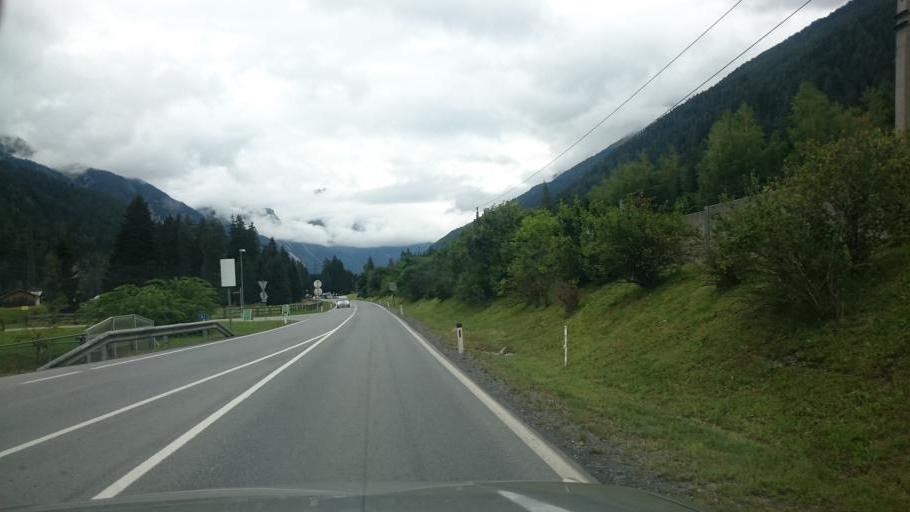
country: AT
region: Tyrol
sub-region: Politischer Bezirk Landeck
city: Sankt Anton am Arlberg
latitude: 47.1421
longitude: 10.3022
